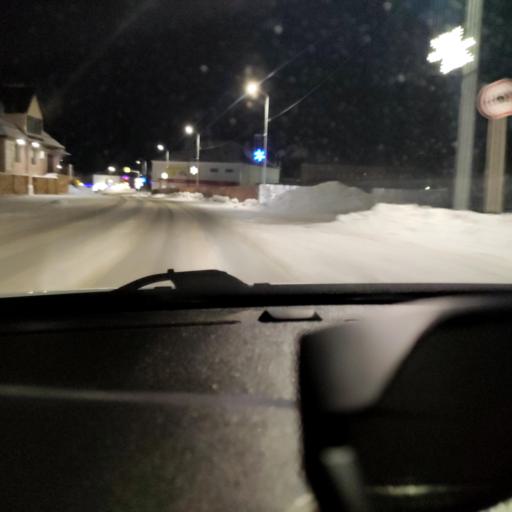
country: RU
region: Tatarstan
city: Vysokaya Gora
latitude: 55.9305
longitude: 49.3045
